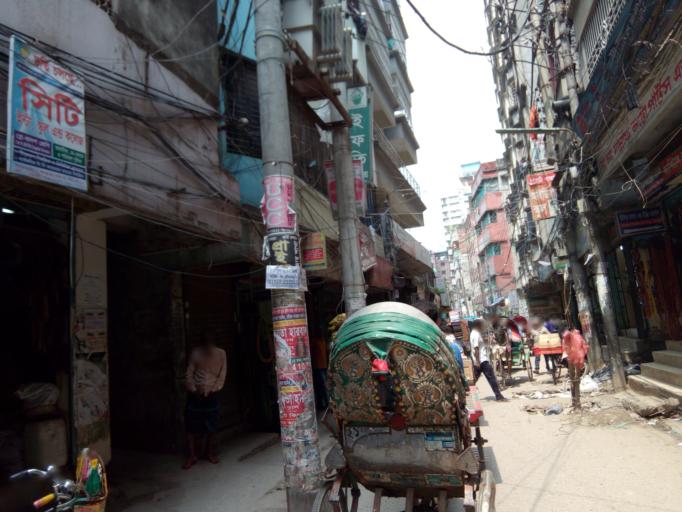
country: BD
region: Dhaka
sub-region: Dhaka
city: Dhaka
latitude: 23.7211
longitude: 90.4143
